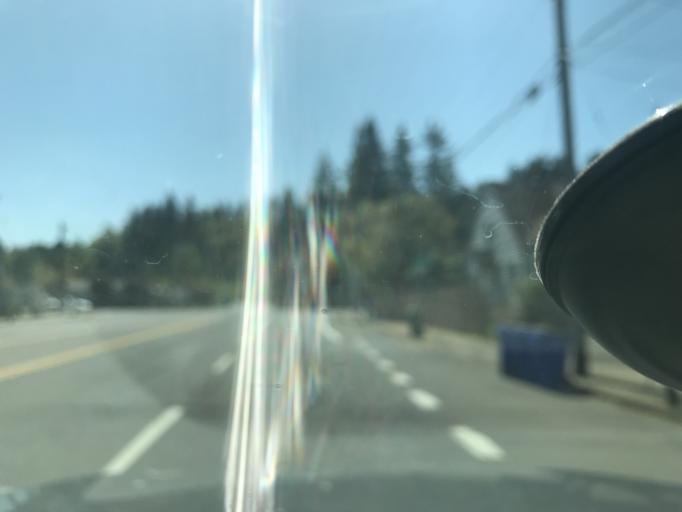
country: US
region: Oregon
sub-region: Clackamas County
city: Happy Valley
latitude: 45.4956
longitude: -122.4969
